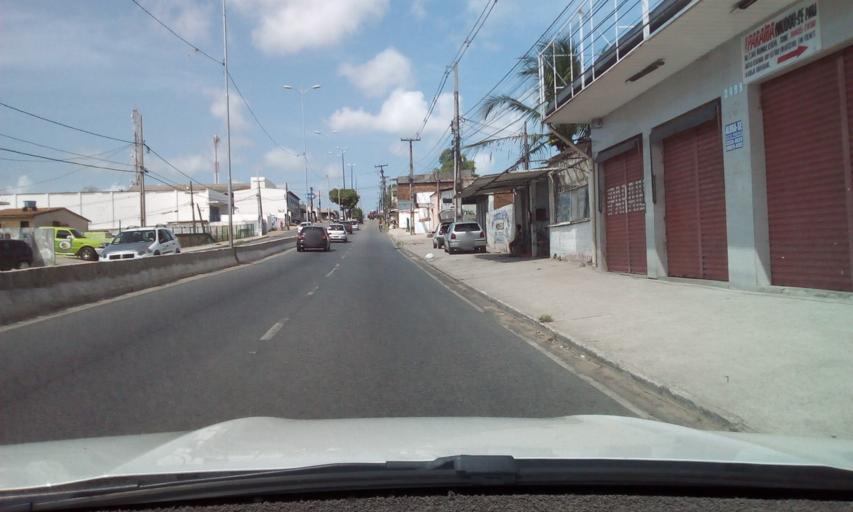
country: BR
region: Paraiba
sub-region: Bayeux
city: Bayeux
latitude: -7.1533
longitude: -34.8949
